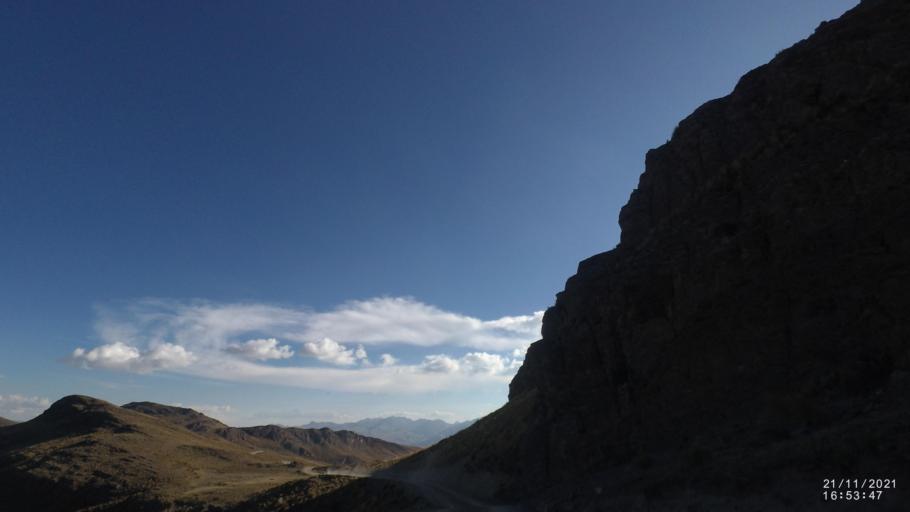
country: BO
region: Cochabamba
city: Cochabamba
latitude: -17.0874
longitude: -66.2543
